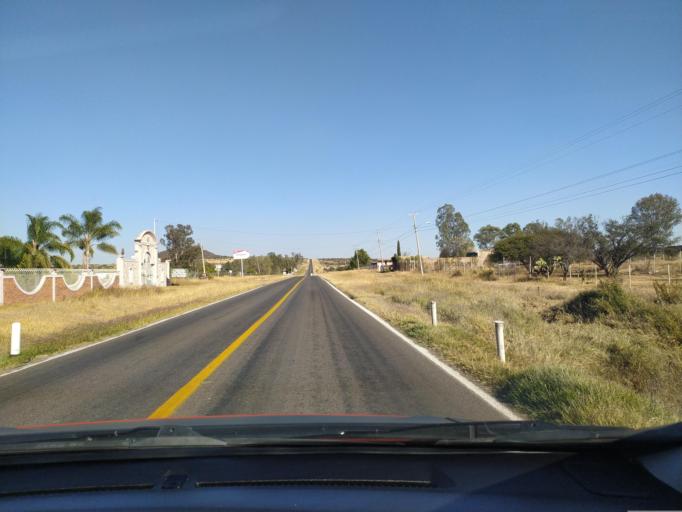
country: MX
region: Jalisco
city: San Miguel el Alto
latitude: 21.0209
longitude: -102.4502
